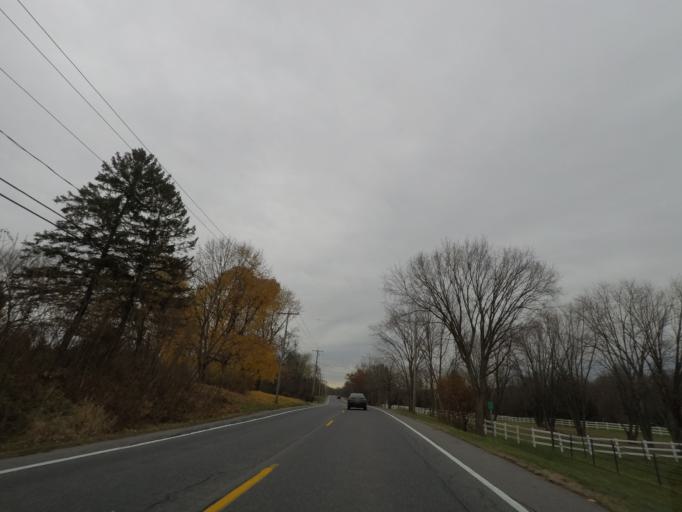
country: US
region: New York
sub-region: Saratoga County
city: Country Knolls
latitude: 42.8923
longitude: -73.8410
